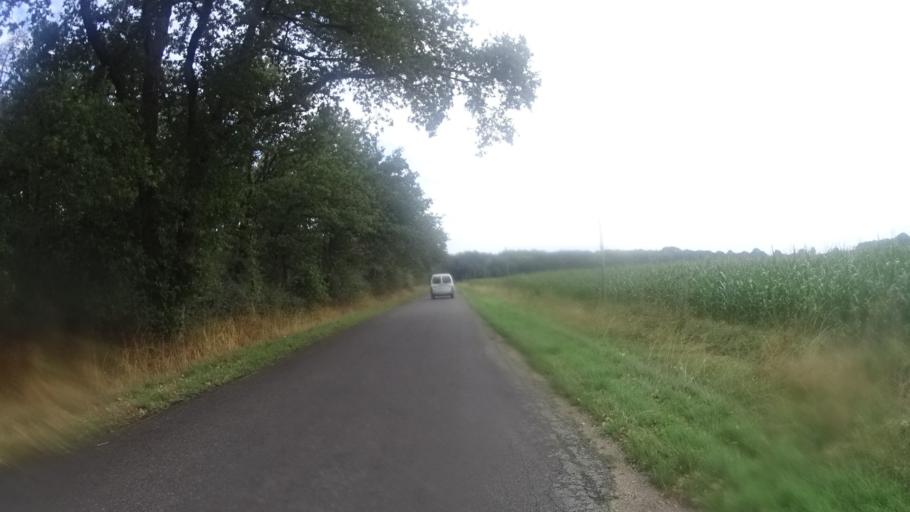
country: FR
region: Centre
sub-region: Departement du Loiret
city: Chateauneuf-sur-Loire
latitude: 47.8995
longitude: 2.2114
